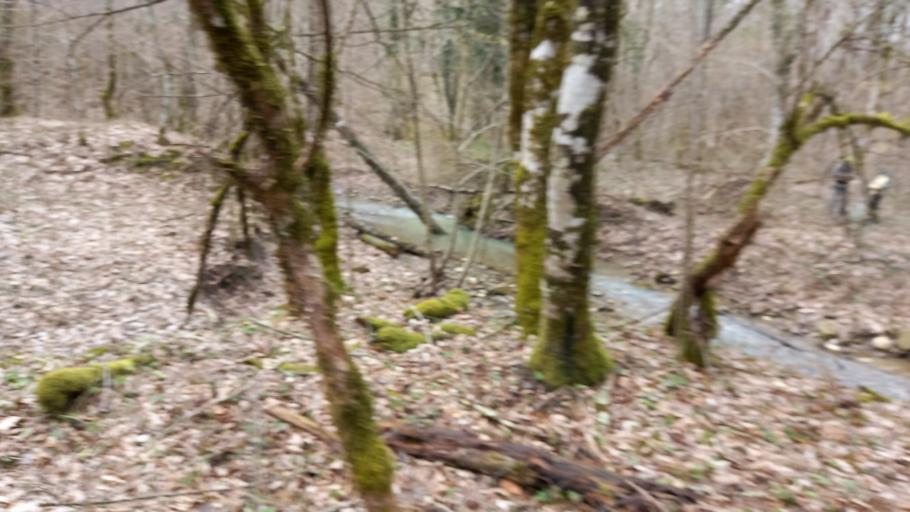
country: RU
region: Krasnodarskiy
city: Pshada
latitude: 44.4922
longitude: 38.3890
